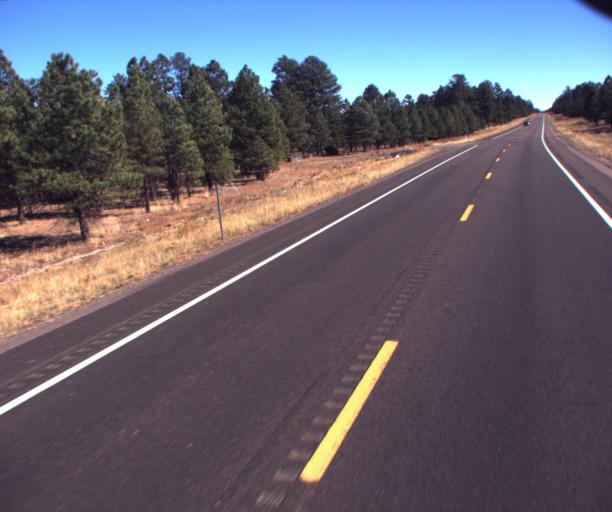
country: US
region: Arizona
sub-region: Apache County
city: Saint Michaels
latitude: 35.6976
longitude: -109.2799
